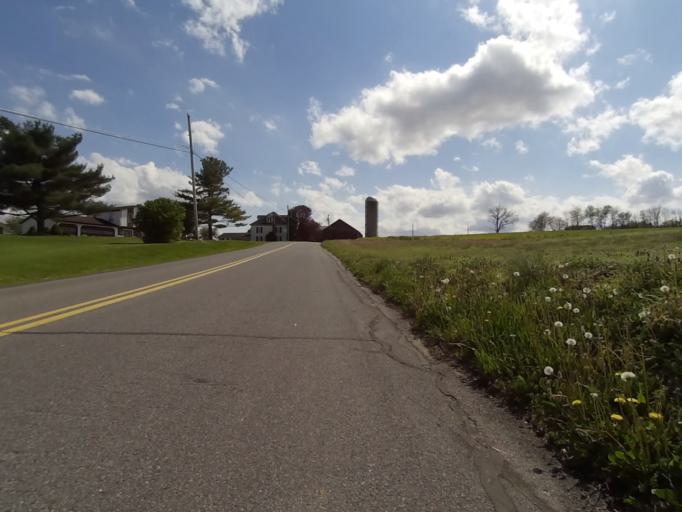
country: US
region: Pennsylvania
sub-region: Centre County
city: Bellefonte
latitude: 40.8889
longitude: -77.8067
